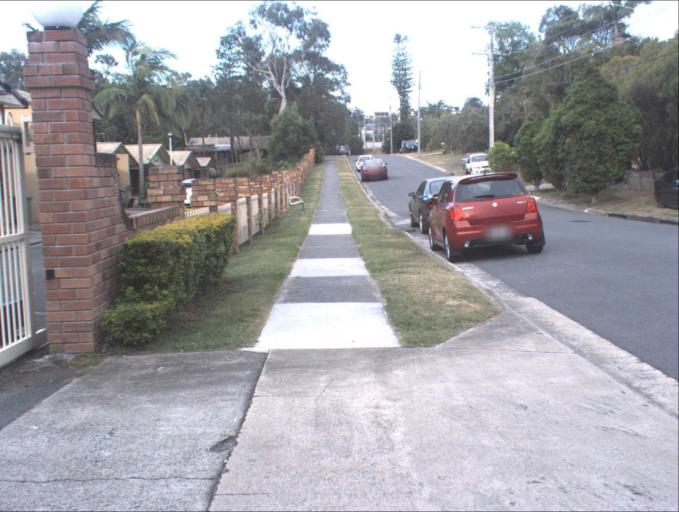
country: AU
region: Queensland
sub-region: Logan
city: Springwood
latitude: -27.6165
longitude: 153.1287
